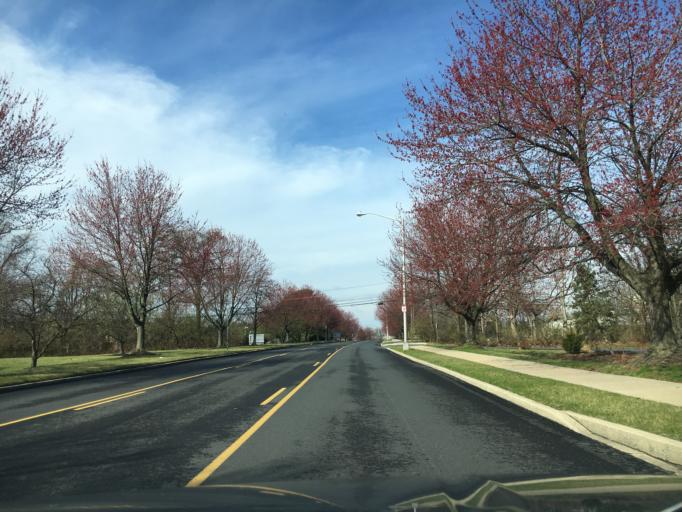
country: US
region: Pennsylvania
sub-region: Northampton County
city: Bethlehem
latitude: 40.6730
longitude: -75.3779
